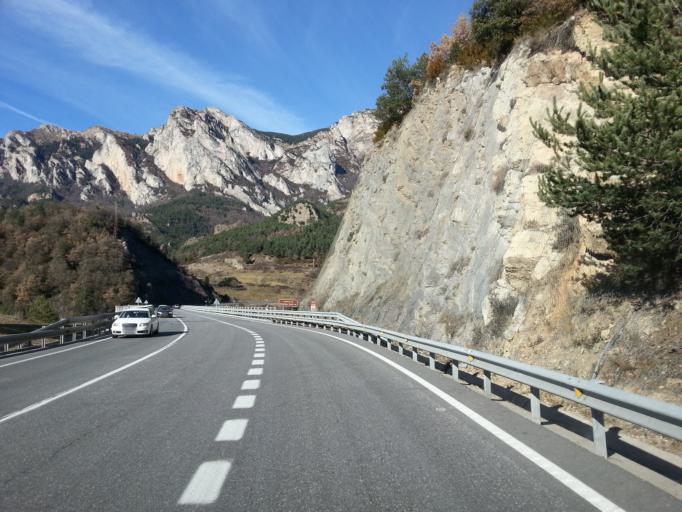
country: ES
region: Catalonia
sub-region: Provincia de Barcelona
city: Baga
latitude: 42.2813
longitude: 1.8530
